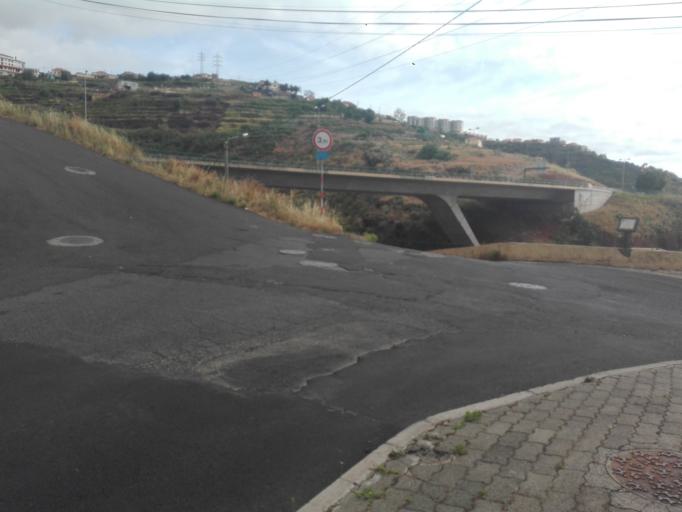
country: PT
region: Madeira
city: Canico
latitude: 32.6498
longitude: -16.8254
